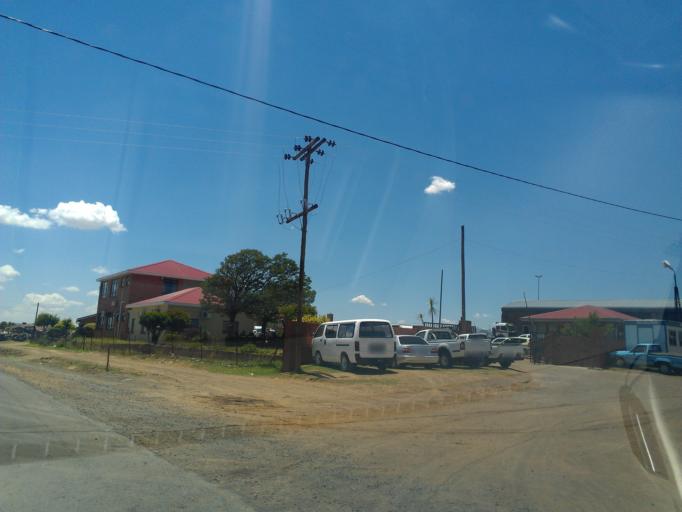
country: LS
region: Berea
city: Teyateyaneng
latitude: -29.1403
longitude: 27.7642
